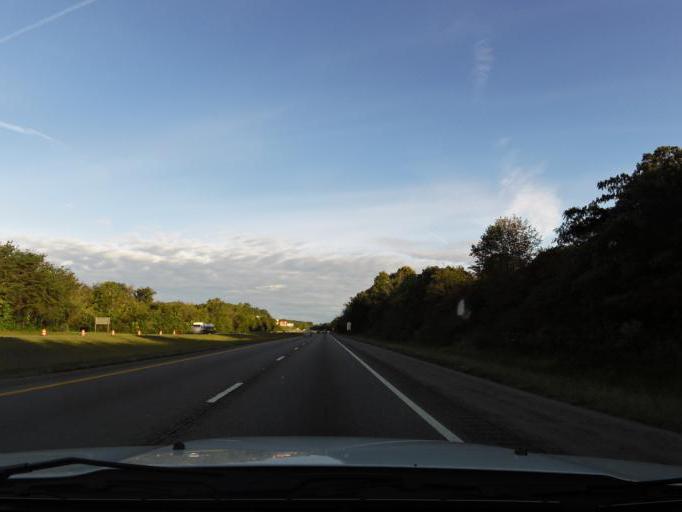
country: US
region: Tennessee
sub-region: Anderson County
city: Norris
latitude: 36.1750
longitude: -84.0886
